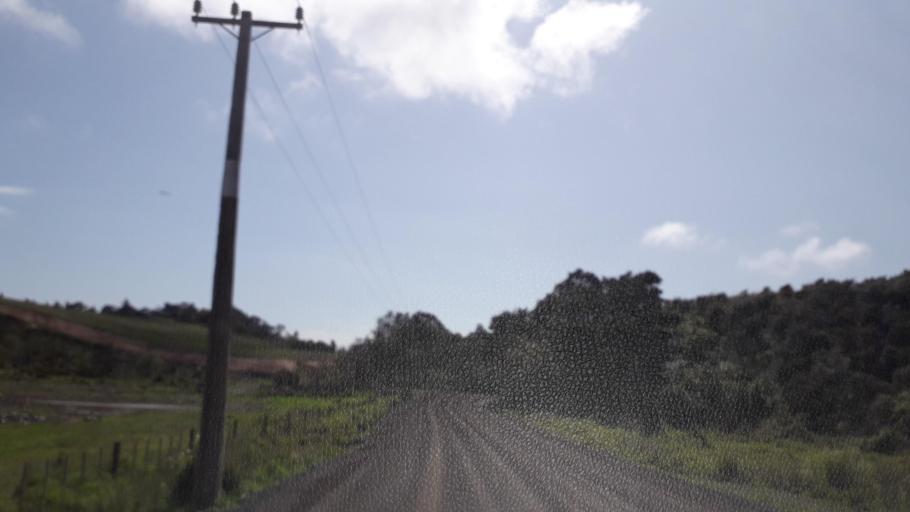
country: NZ
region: Northland
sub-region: Far North District
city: Paihia
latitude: -35.2391
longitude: 174.2489
